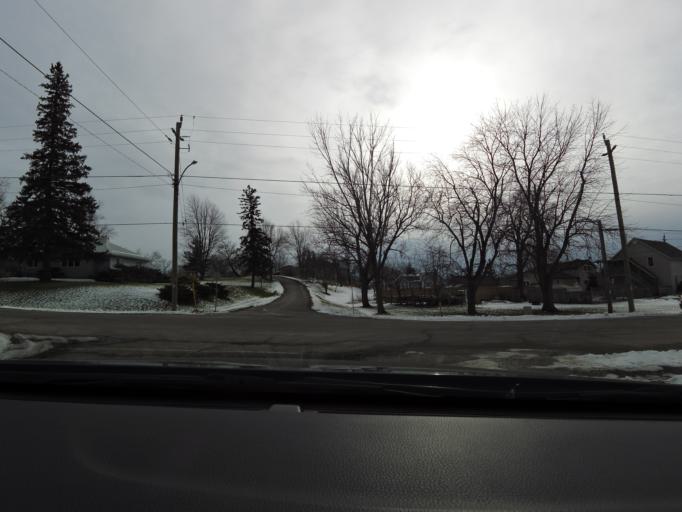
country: CA
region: Ontario
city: Ancaster
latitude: 43.0210
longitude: -79.8895
